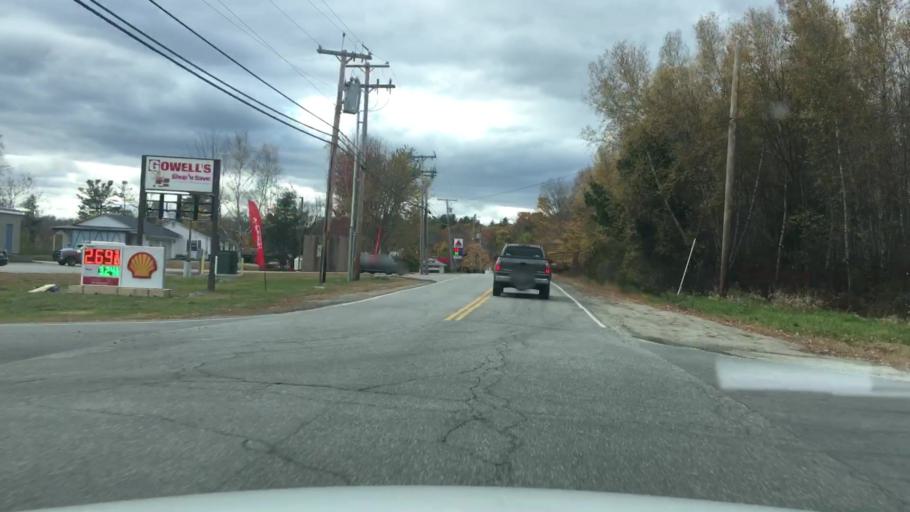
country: US
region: Maine
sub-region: Kennebec County
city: Monmouth
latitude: 44.1351
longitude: -69.9779
